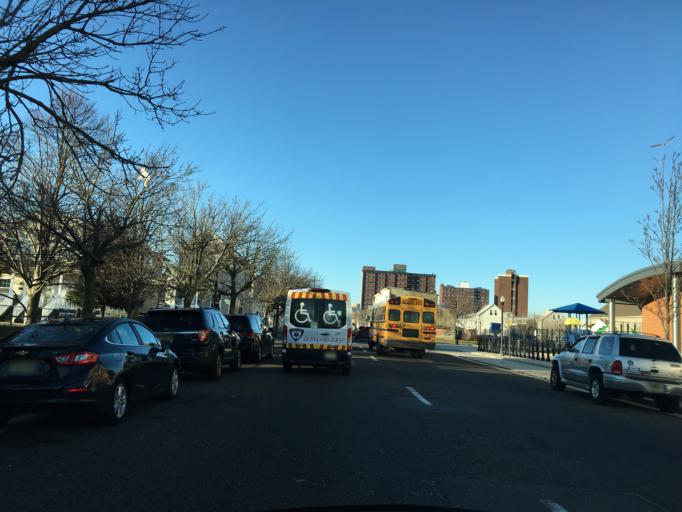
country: US
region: New Jersey
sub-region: Atlantic County
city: Atlantic City
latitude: 39.3669
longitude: -74.4252
